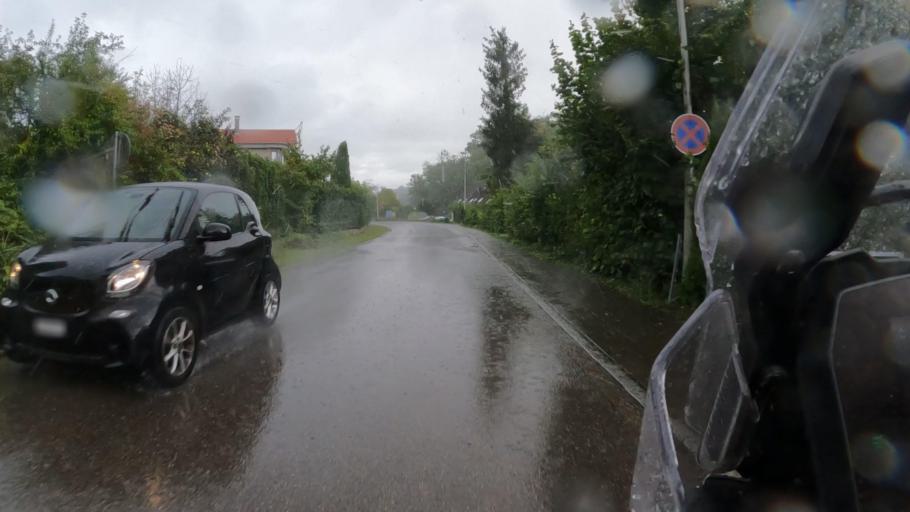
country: DE
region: Baden-Wuerttemberg
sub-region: Freiburg Region
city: Jestetten
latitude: 47.6487
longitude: 8.5706
